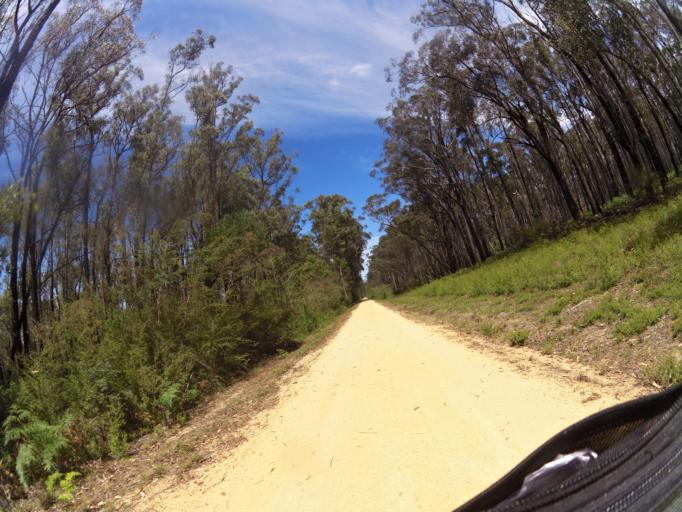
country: AU
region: Victoria
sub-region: East Gippsland
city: Lakes Entrance
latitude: -37.7320
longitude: 148.0808
